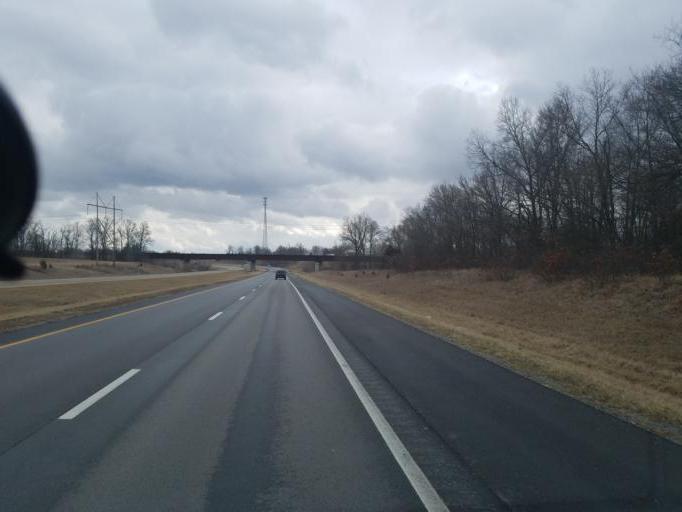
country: US
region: Missouri
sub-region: Randolph County
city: Moberly
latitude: 39.2981
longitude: -92.3736
